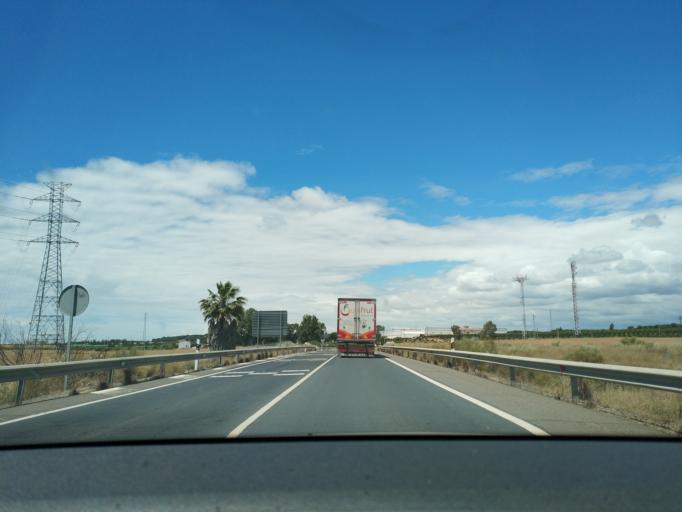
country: ES
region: Andalusia
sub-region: Provincia de Huelva
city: Aljaraque
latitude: 37.3200
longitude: -7.0722
